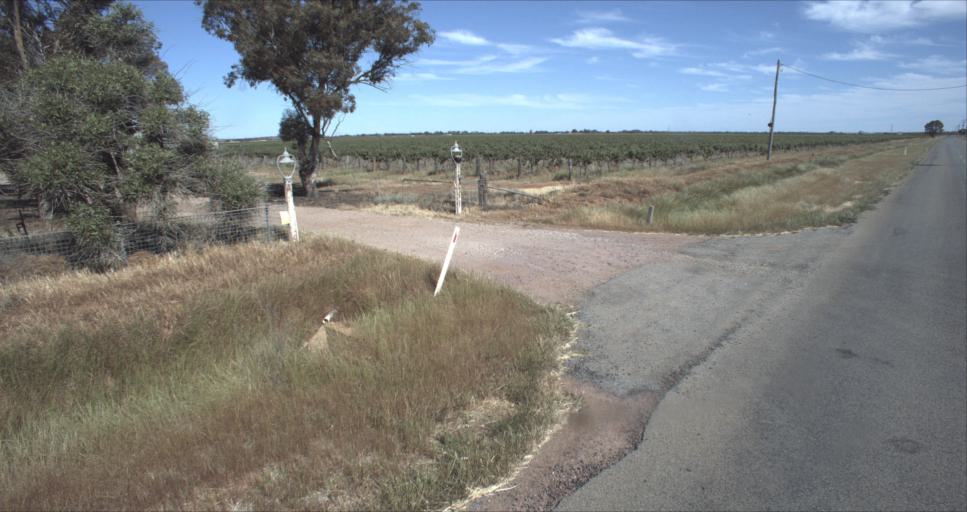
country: AU
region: New South Wales
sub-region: Leeton
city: Leeton
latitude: -34.5735
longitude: 146.3812
